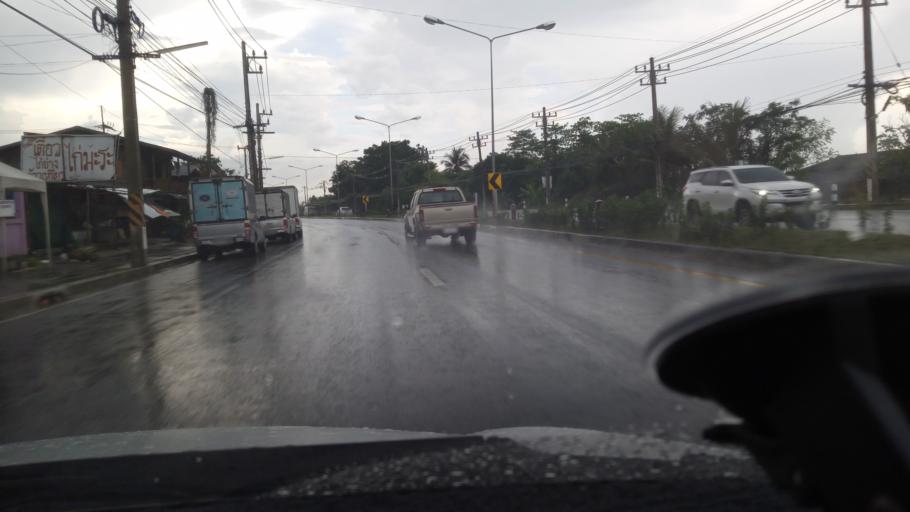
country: TH
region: Chon Buri
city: Phan Thong
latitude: 13.4493
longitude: 101.0995
